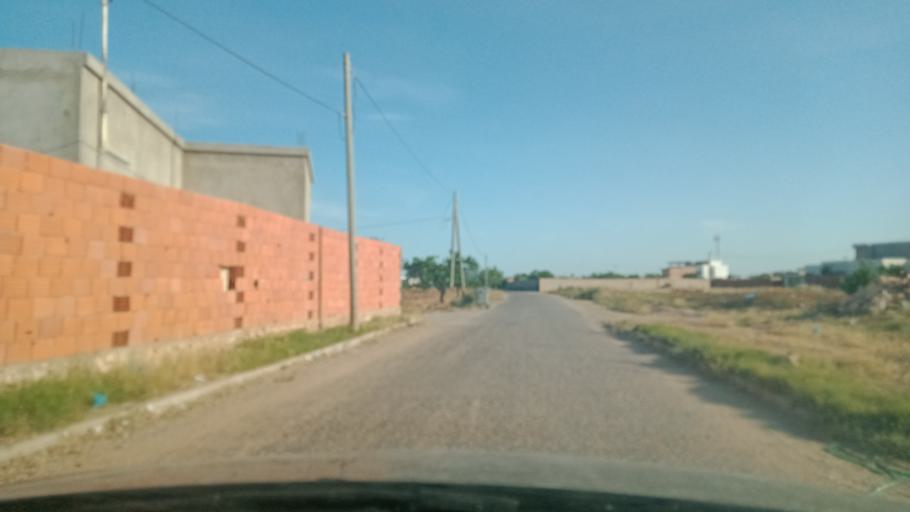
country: TN
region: Safaqis
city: Sfax
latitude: 34.8223
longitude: 10.7357
